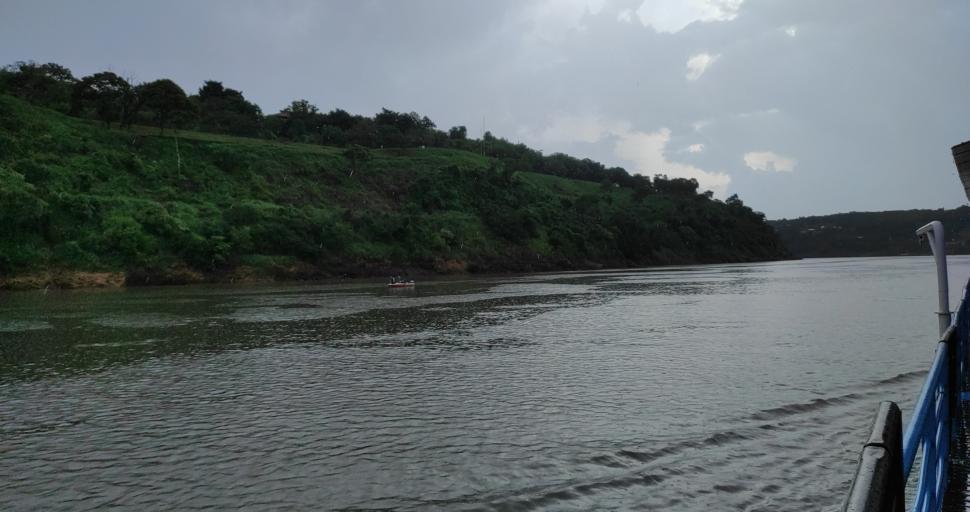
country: AR
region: Misiones
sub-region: Departamento de Iguazu
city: Puerto Iguazu
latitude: -25.5928
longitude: -54.5842
